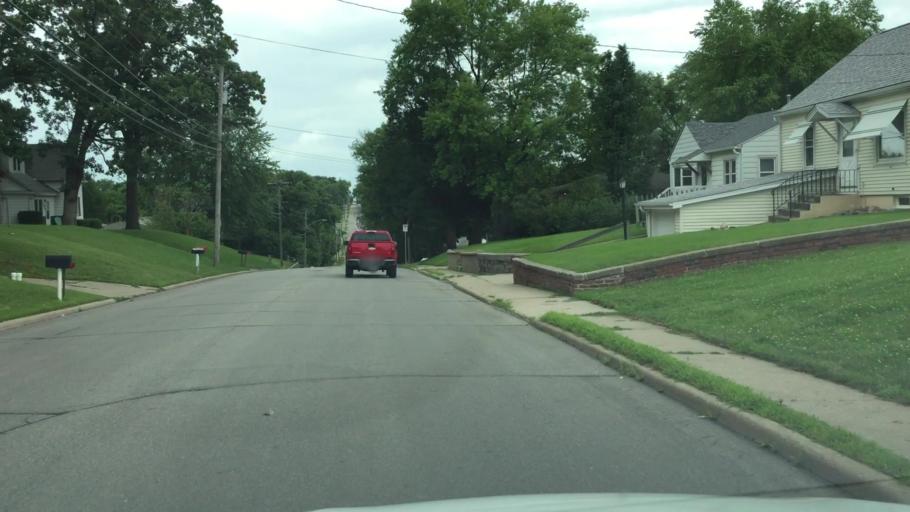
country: US
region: Iowa
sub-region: Jasper County
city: Newton
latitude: 41.7078
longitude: -93.0532
